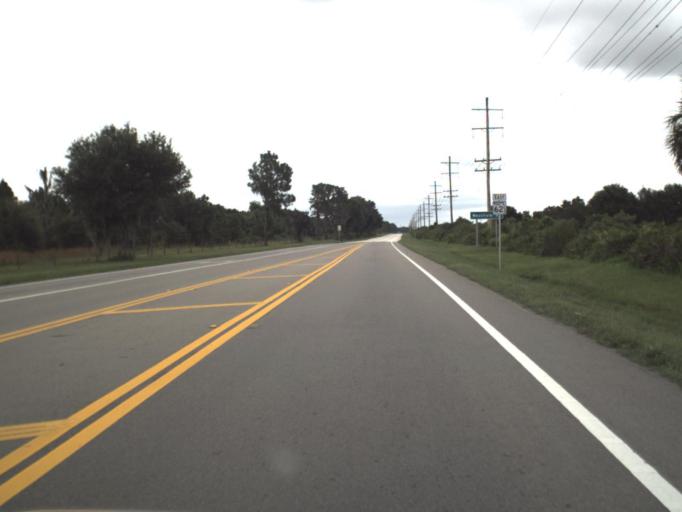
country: US
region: Florida
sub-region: Hillsborough County
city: Wimauma
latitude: 27.5900
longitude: -82.1189
